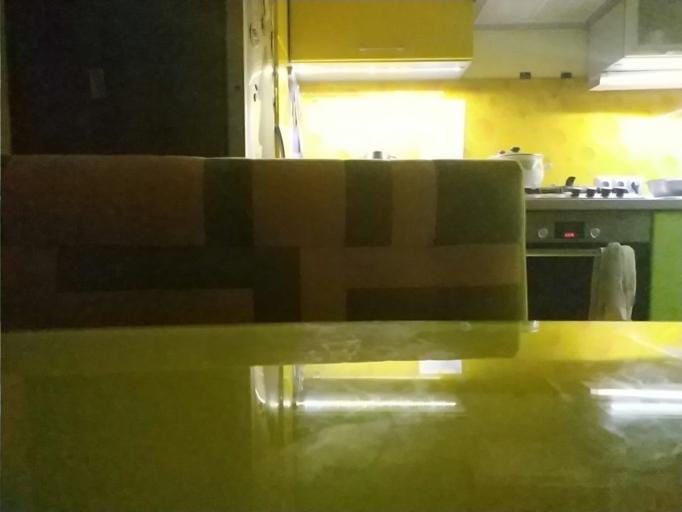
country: RU
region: Republic of Karelia
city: Pyaozerskiy
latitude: 65.8842
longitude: 30.4345
